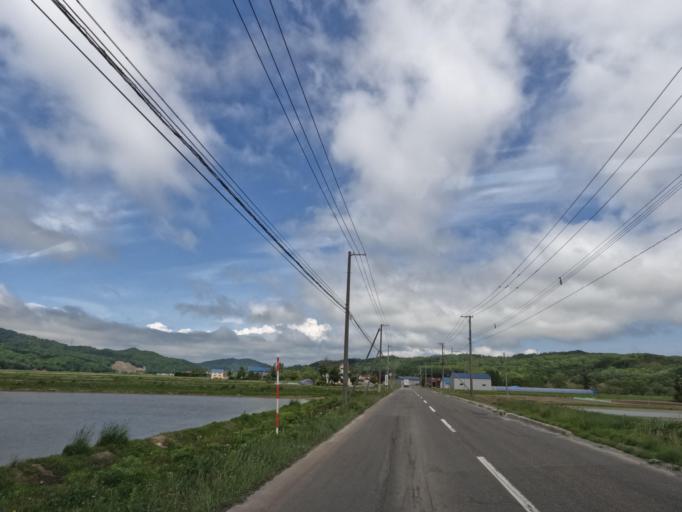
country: JP
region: Hokkaido
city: Tobetsu
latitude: 43.2730
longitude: 141.5319
